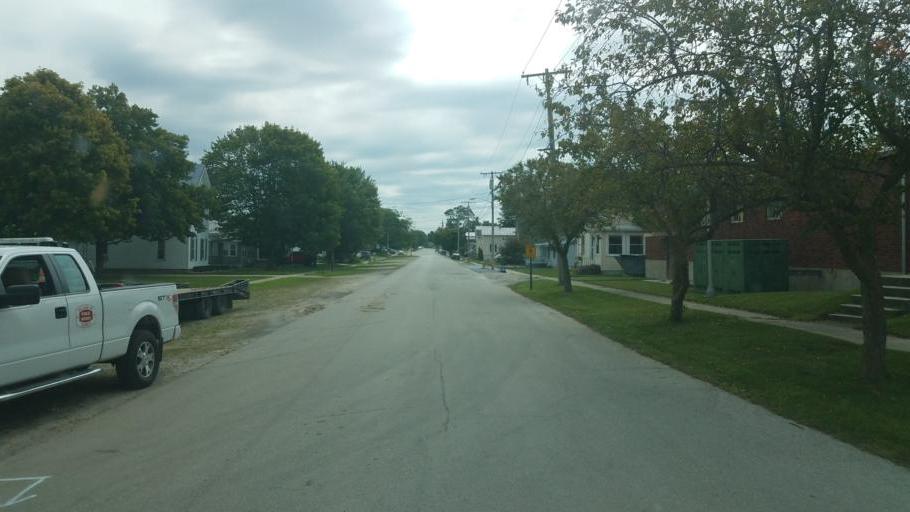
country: US
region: Ohio
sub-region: Wyandot County
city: Carey
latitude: 40.9518
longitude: -83.3864
